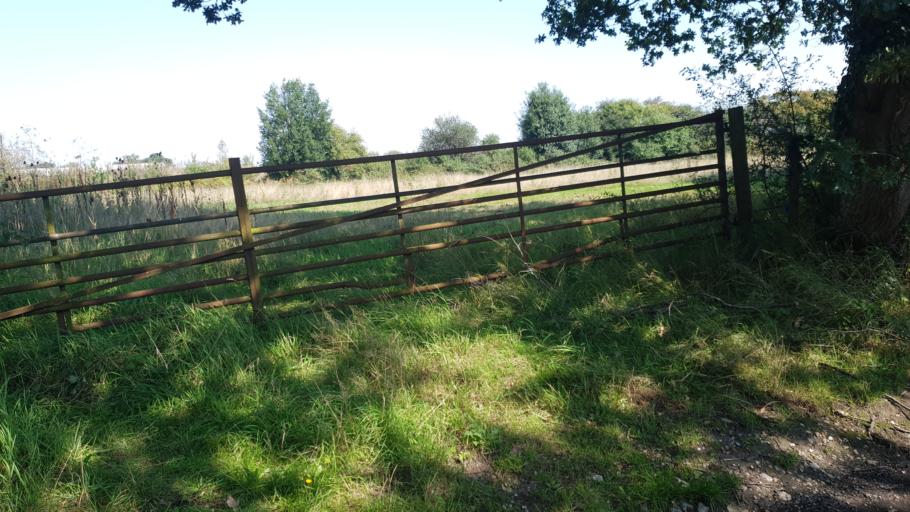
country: GB
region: England
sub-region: Essex
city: Colchester
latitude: 51.9242
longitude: 0.9417
